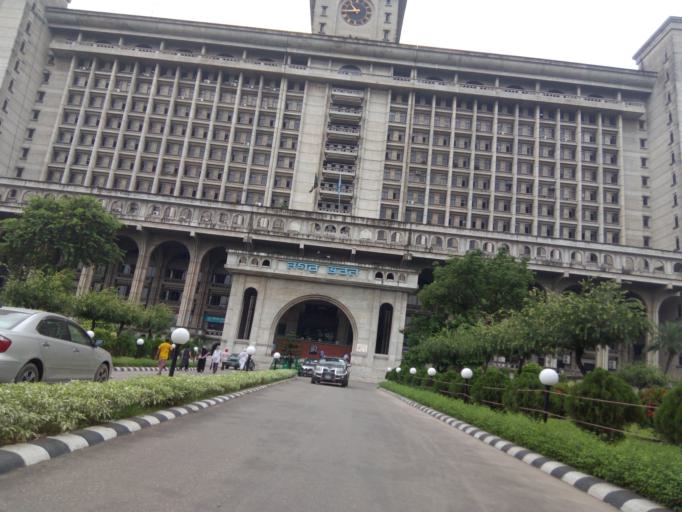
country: BD
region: Dhaka
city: Paltan
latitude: 23.7247
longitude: 90.4084
